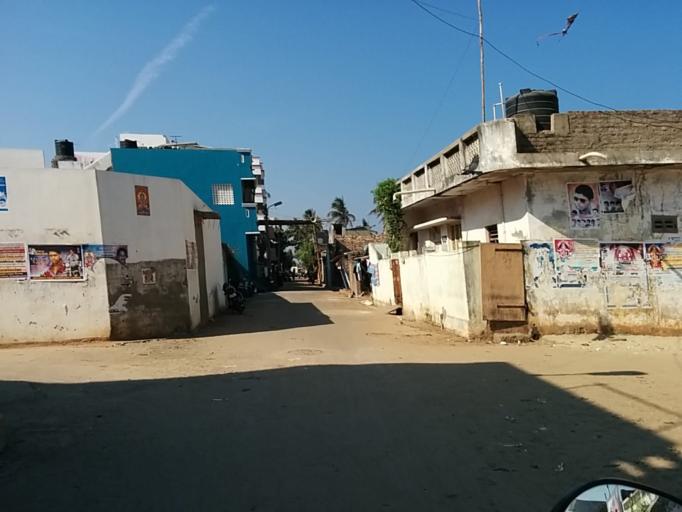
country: IN
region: Pondicherry
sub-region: Puducherry
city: Puducherry
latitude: 11.9448
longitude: 79.8374
